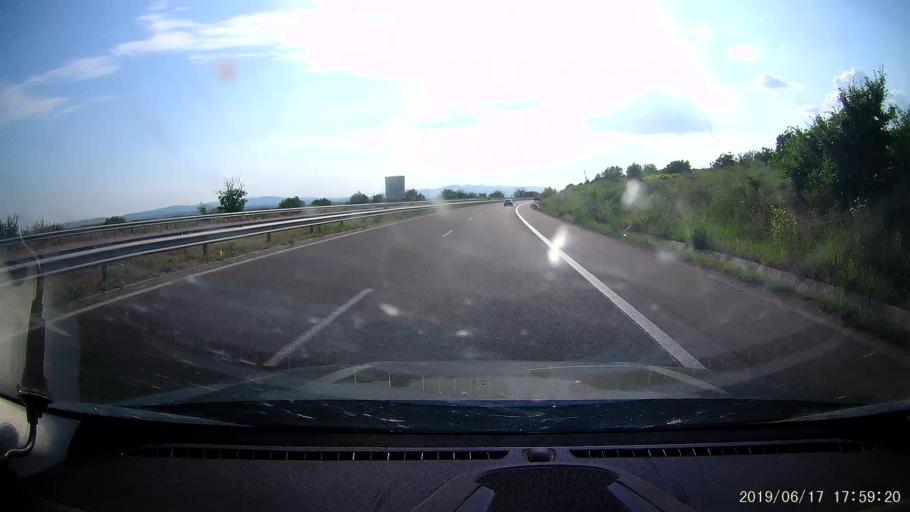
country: BG
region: Khaskovo
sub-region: Obshtina Svilengrad
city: Svilengrad
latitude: 41.7244
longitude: 26.3004
